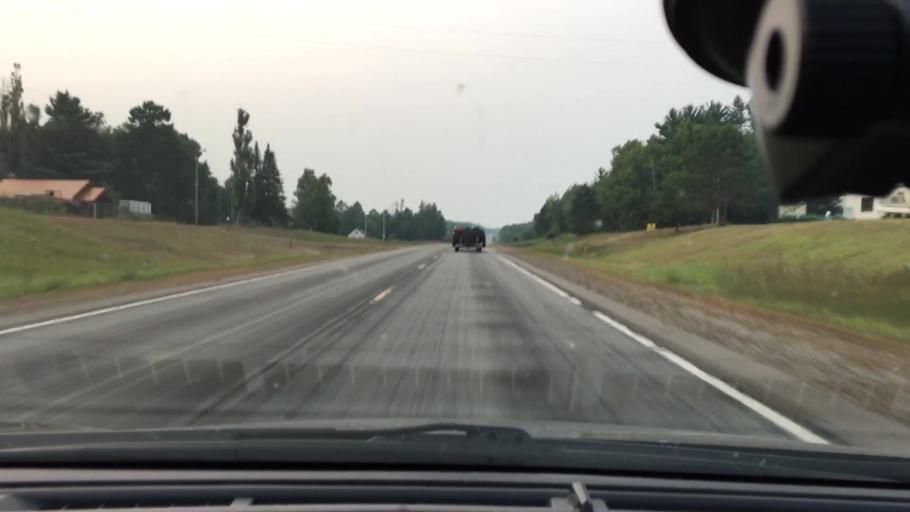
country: US
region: Minnesota
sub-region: Crow Wing County
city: Cross Lake
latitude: 46.6858
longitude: -93.9538
